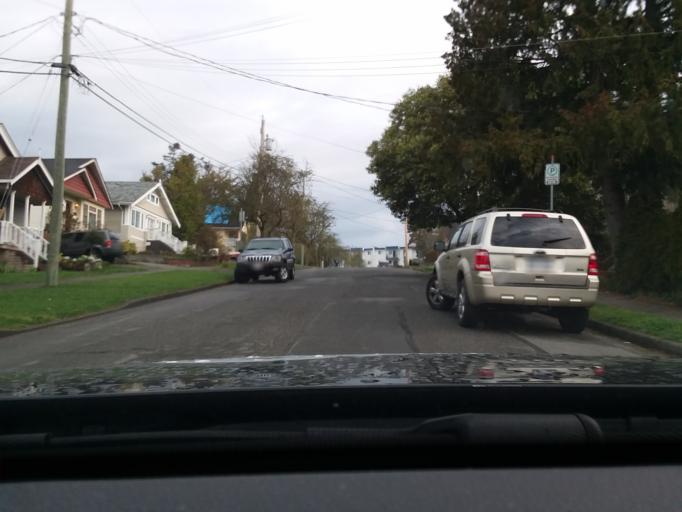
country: CA
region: British Columbia
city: Victoria
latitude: 48.4391
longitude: -123.3971
